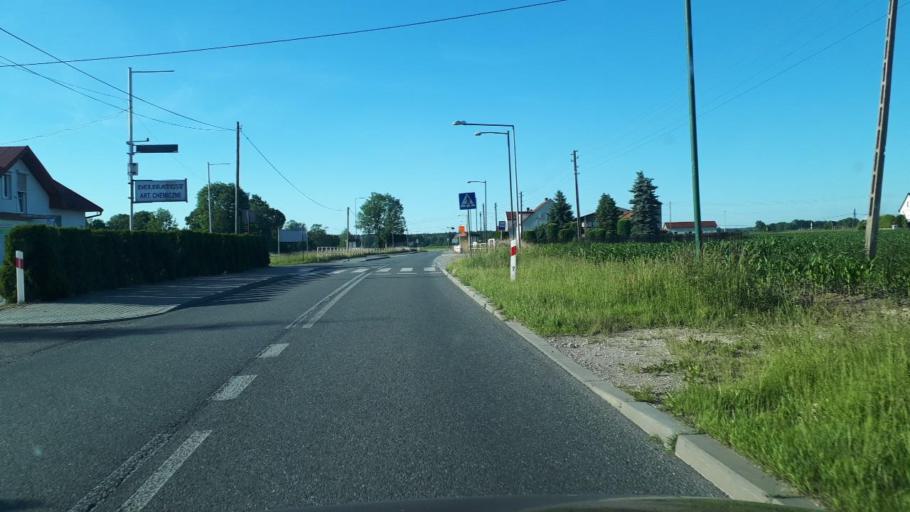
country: PL
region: Opole Voivodeship
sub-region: Powiat oleski
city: Dobrodzien
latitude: 50.6881
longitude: 18.4587
